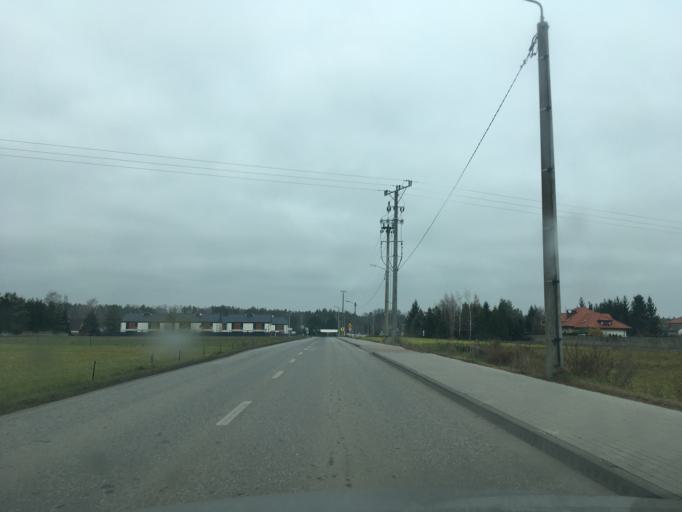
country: PL
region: Masovian Voivodeship
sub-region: Powiat piaseczynski
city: Lesznowola
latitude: 52.0718
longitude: 20.9352
